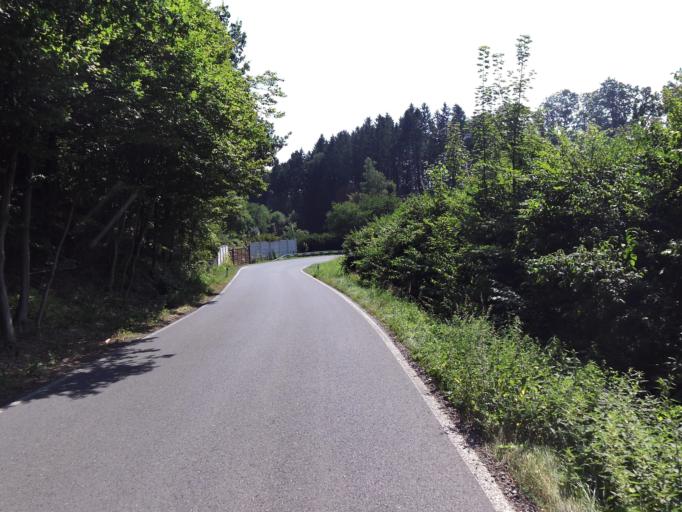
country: CZ
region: Central Bohemia
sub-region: Okres Praha-Vychod
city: Mnichovice
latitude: 49.9503
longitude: 14.7402
